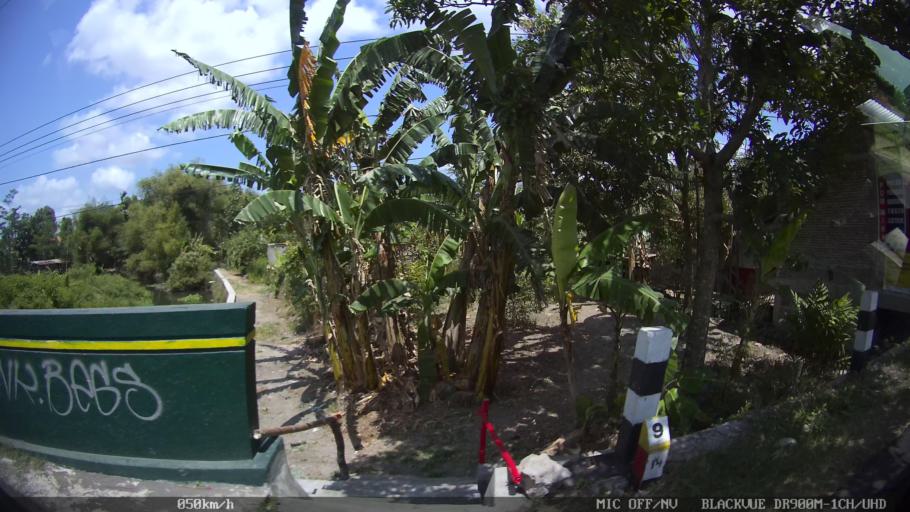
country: ID
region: Daerah Istimewa Yogyakarta
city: Sewon
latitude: -7.9128
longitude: 110.3670
